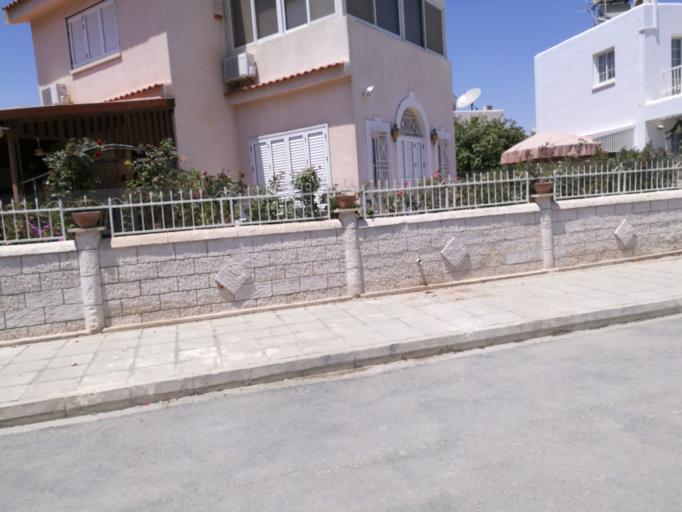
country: CY
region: Larnaka
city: Voroklini
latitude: 34.9697
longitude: 33.6709
